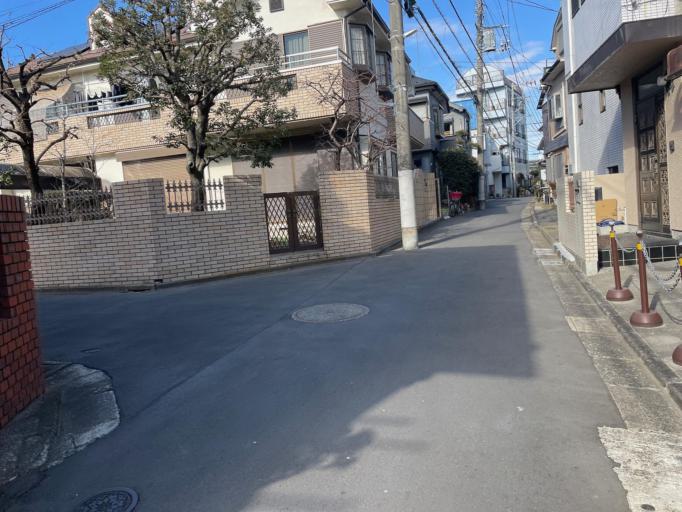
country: JP
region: Saitama
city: Wako
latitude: 35.7587
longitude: 139.6492
